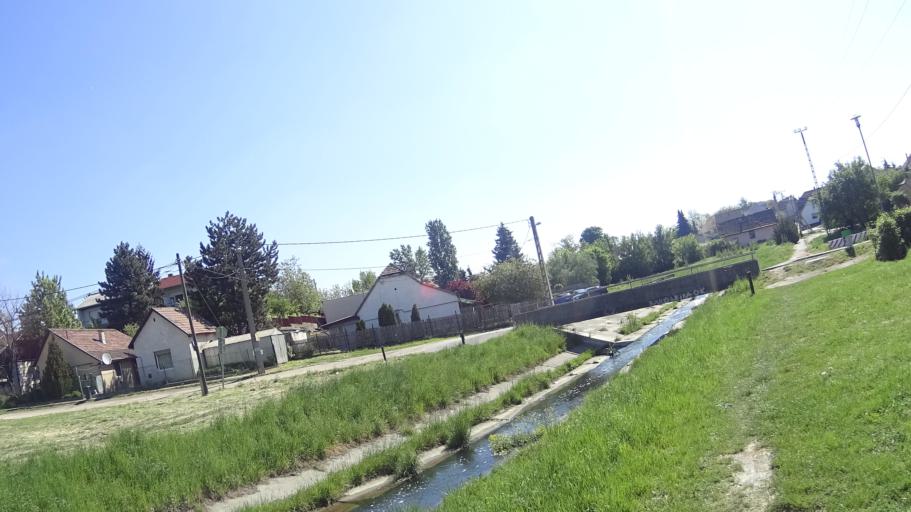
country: HU
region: Budapest
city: Budapest XXIII. keruelet
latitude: 47.3946
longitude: 19.1113
